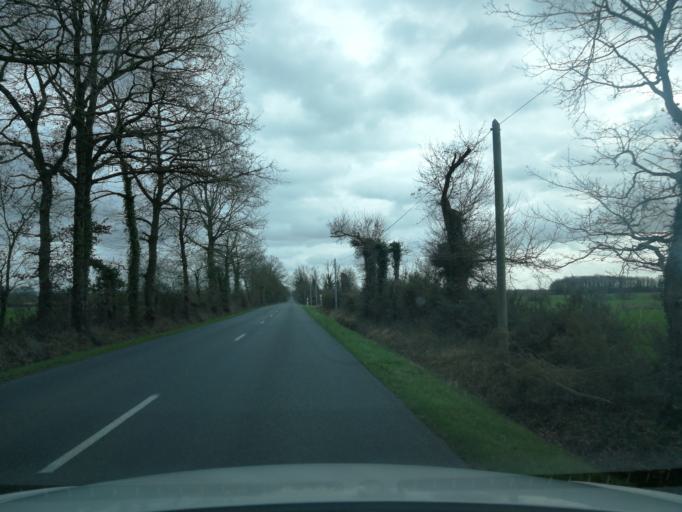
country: FR
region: Pays de la Loire
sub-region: Departement de la Loire-Atlantique
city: Montbert
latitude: 47.0289
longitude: -1.4980
